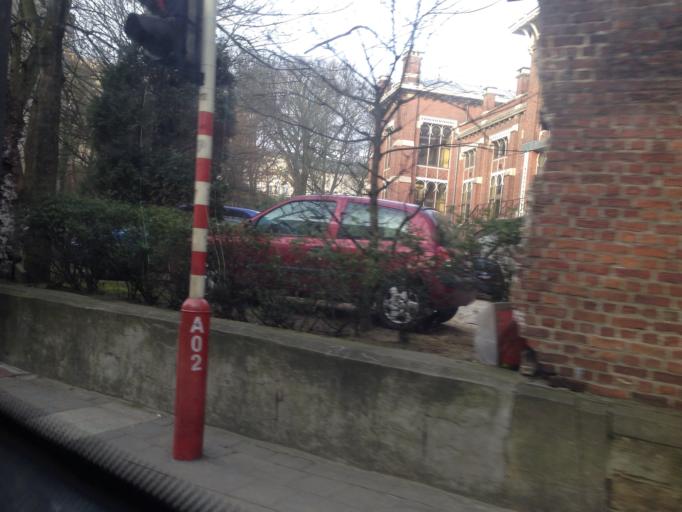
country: BE
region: Brussels Capital
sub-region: Bruxelles-Capitale
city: Brussels
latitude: 50.8377
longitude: 4.3808
